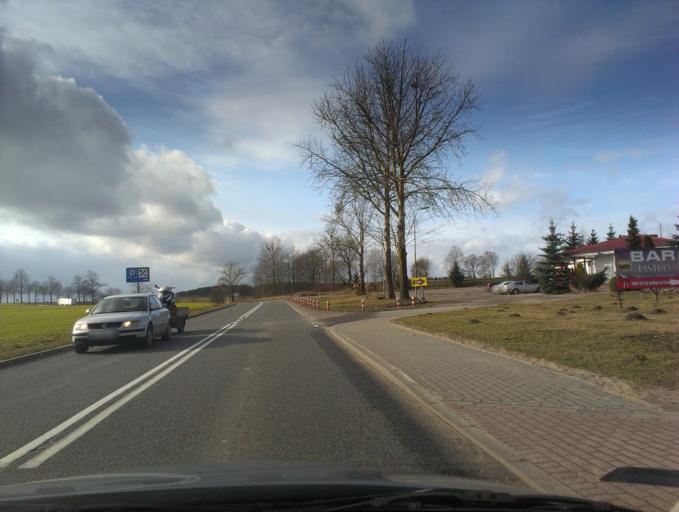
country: PL
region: Pomeranian Voivodeship
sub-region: Powiat czluchowski
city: Debrzno
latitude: 53.6258
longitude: 17.2251
